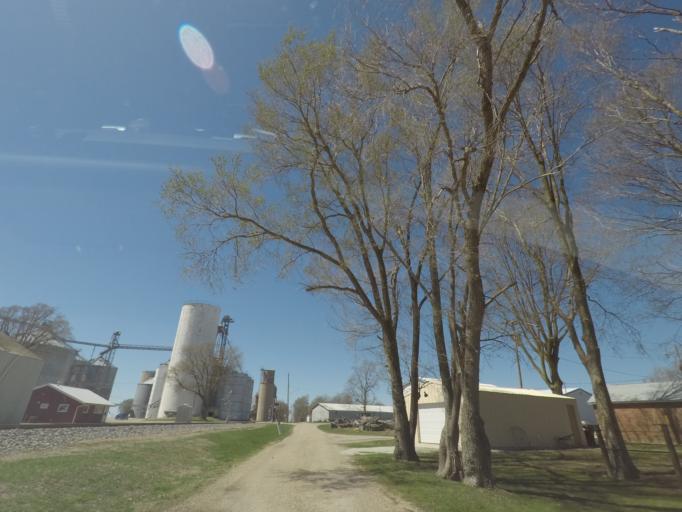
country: US
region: Illinois
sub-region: Macon County
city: Warrensburg
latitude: 39.9654
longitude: -89.1606
